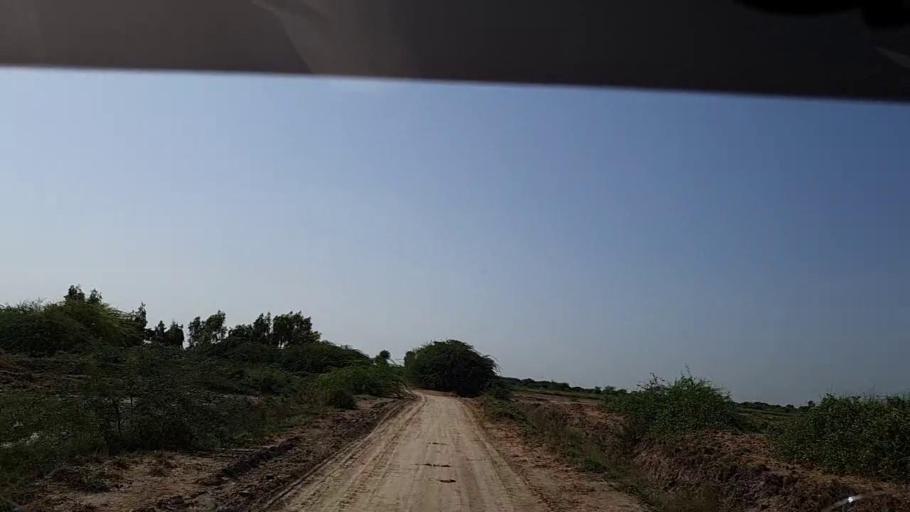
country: PK
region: Sindh
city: Badin
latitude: 24.6209
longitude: 68.7753
